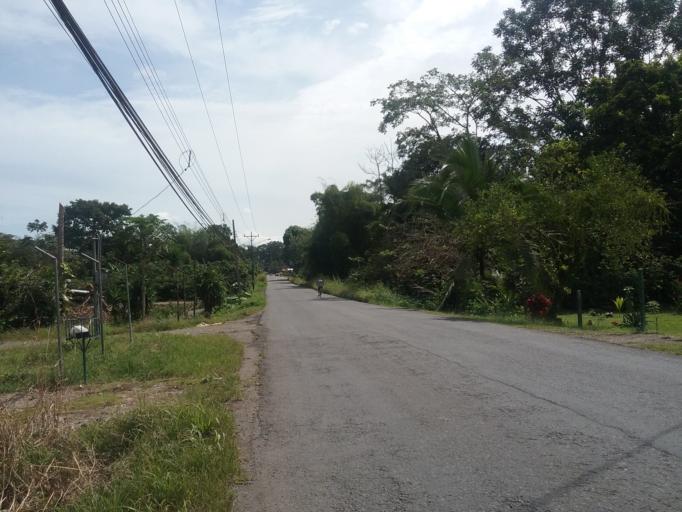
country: CR
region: Limon
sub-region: Canton de Pococi
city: Guapiles
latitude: 10.3204
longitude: -83.8968
